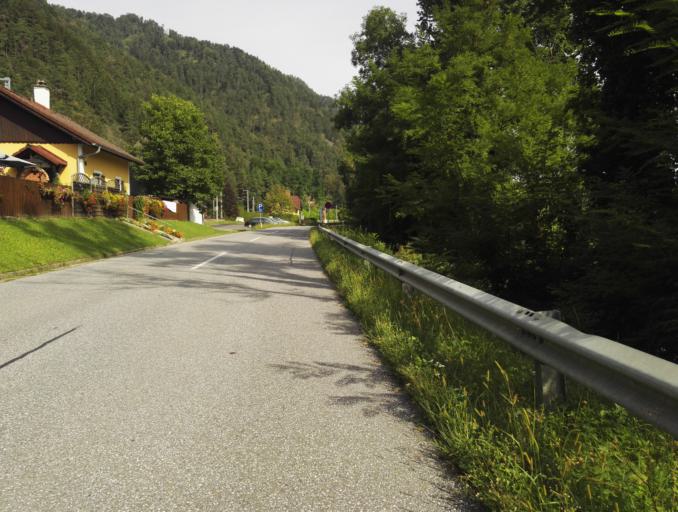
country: AT
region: Styria
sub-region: Politischer Bezirk Graz-Umgebung
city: Deutschfeistritz
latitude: 47.1573
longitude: 15.3164
